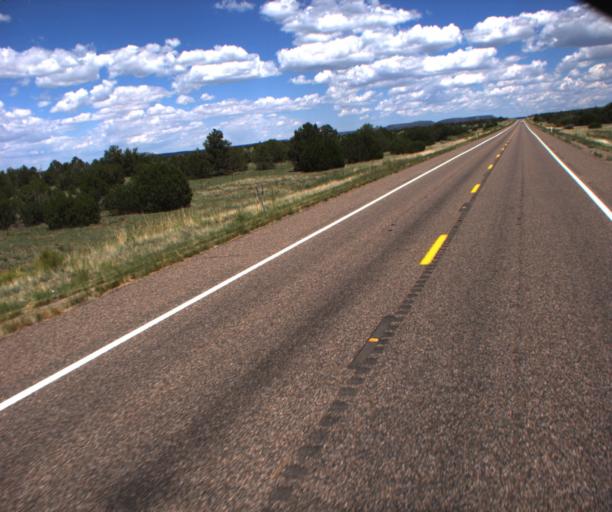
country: US
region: Arizona
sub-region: Apache County
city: Springerville
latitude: 34.1481
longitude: -109.1913
